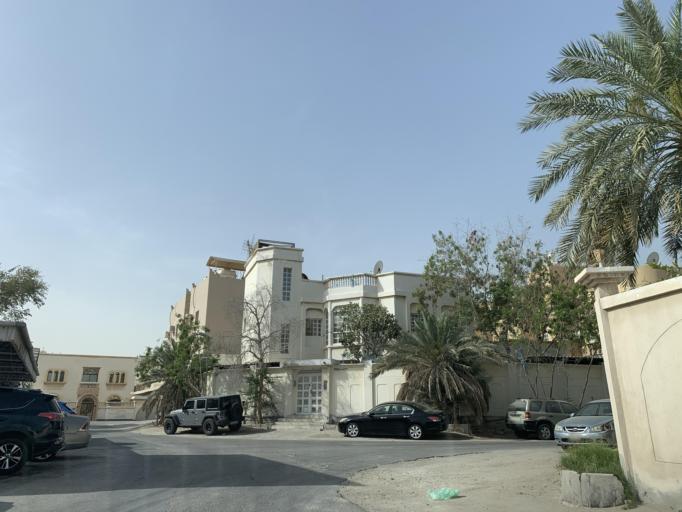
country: BH
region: Northern
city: Madinat `Isa
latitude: 26.1756
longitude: 50.5634
